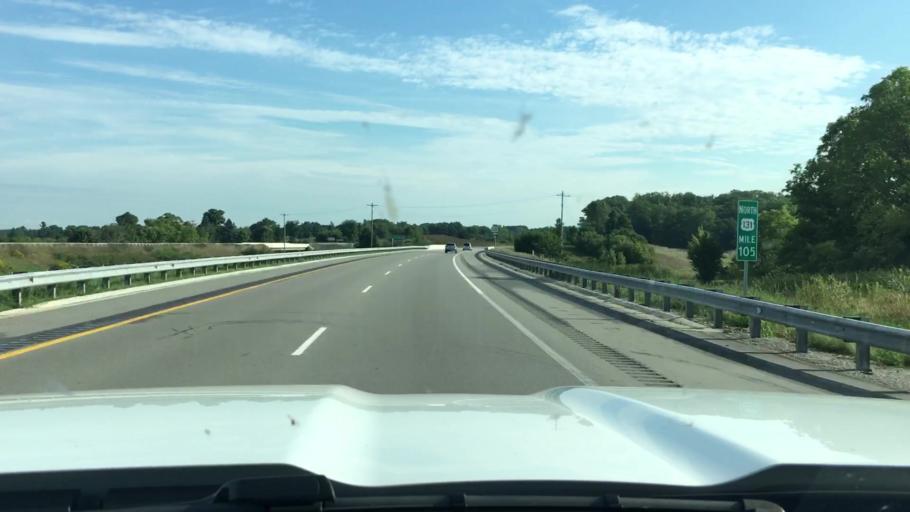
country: US
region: Michigan
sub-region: Kent County
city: Cedar Springs
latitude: 43.2270
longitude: -85.5726
